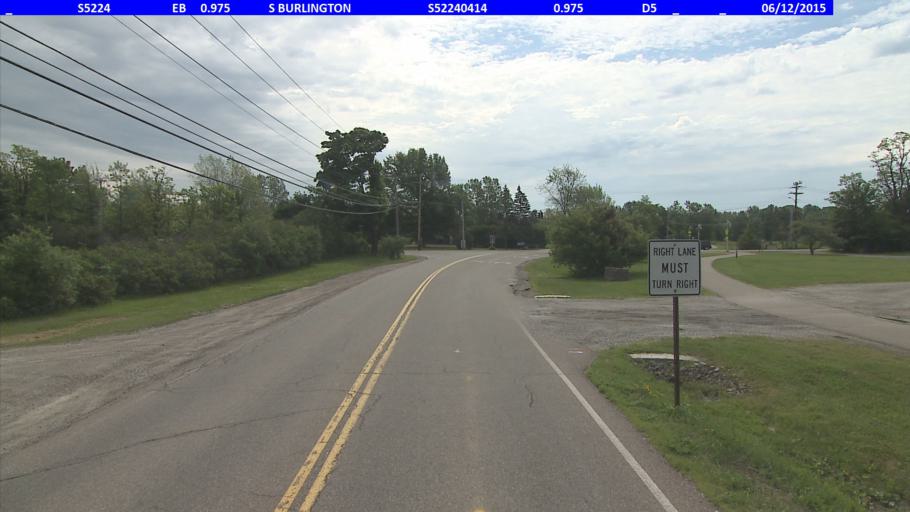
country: US
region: Vermont
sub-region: Chittenden County
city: South Burlington
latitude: 44.4436
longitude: -73.1899
